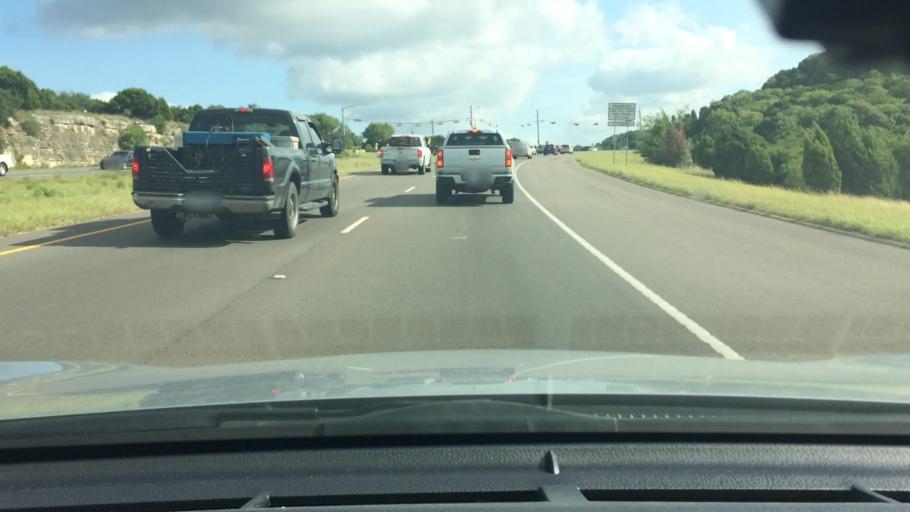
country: US
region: Texas
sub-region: Travis County
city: Lost Creek
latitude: 30.3139
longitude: -97.8266
